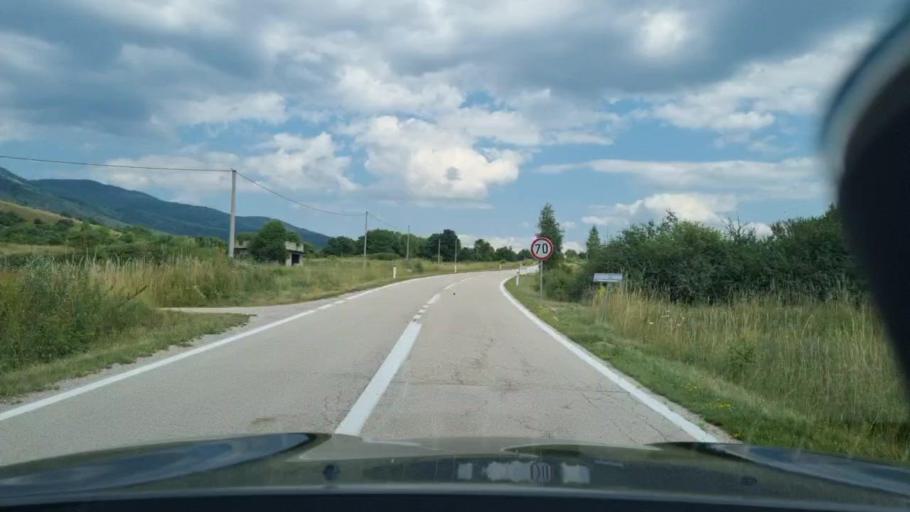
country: BA
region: Federation of Bosnia and Herzegovina
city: Bosansko Grahovo
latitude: 44.1242
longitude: 16.5259
